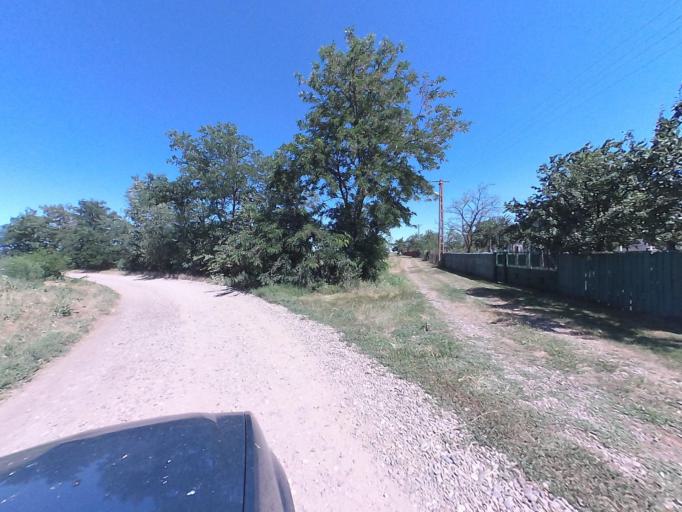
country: RO
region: Vaslui
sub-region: Comuna Costesti
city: Costesti
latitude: 46.4795
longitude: 27.7850
